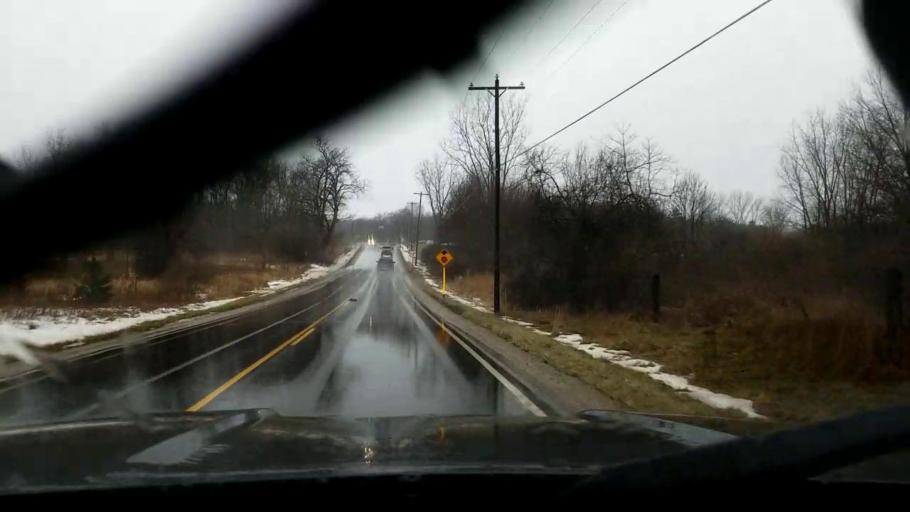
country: US
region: Michigan
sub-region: Jackson County
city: Jackson
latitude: 42.2767
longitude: -84.3813
